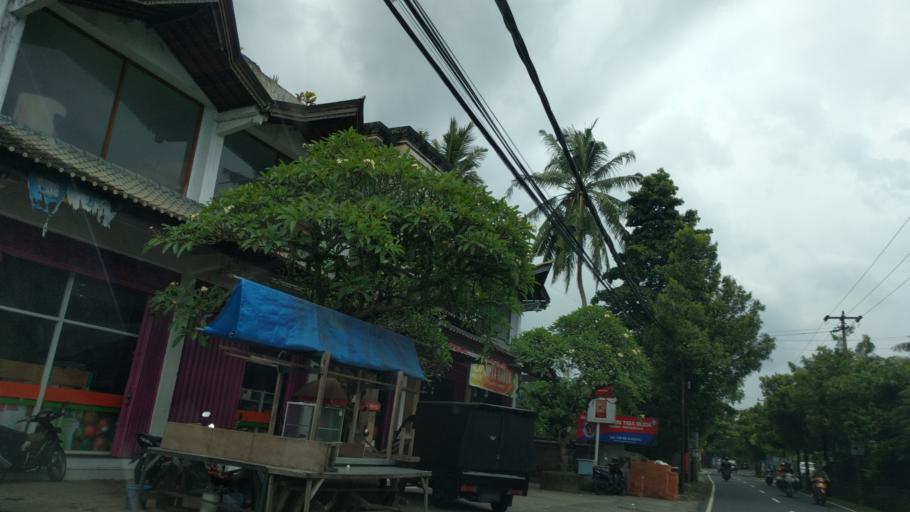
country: ID
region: Bali
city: Banjar Pande
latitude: -8.5158
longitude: 115.2401
